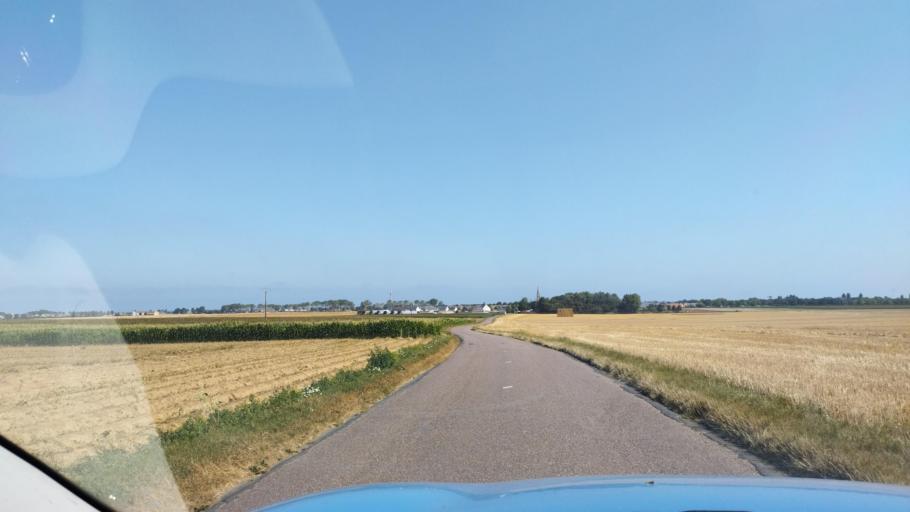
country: FR
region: Lower Normandy
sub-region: Departement du Calvados
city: Saint-Aubin-sur-Mer
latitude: 49.3159
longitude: -0.4026
